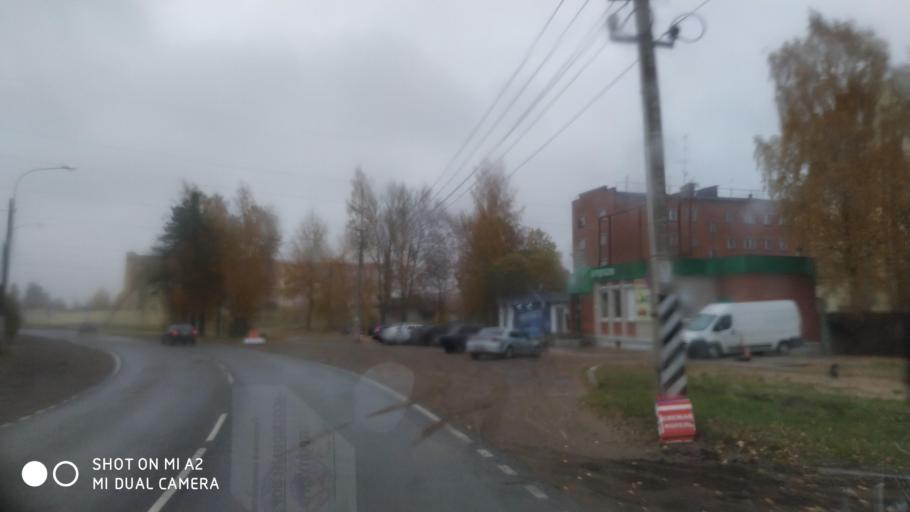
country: RU
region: Leningrad
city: Sosnovyy Bor
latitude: 59.8932
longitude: 29.1102
